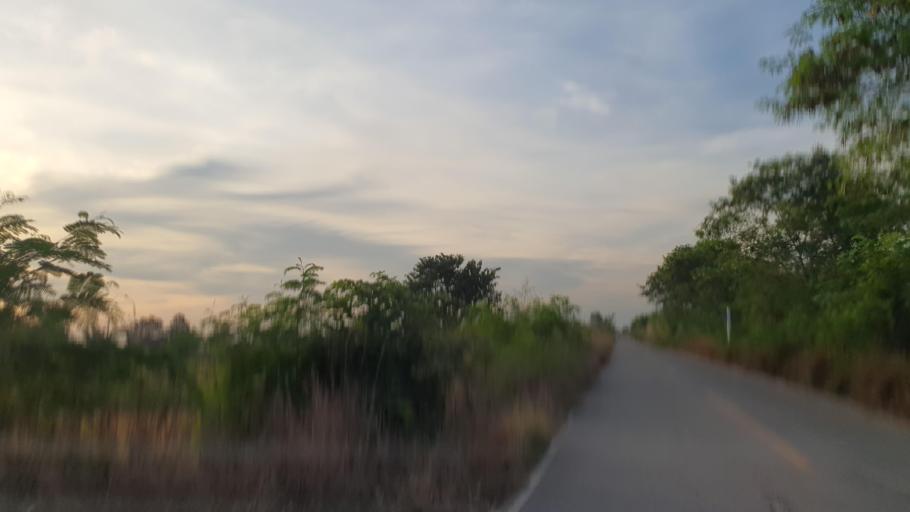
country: TH
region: Uthai Thani
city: Sawang Arom
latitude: 15.6974
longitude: 99.9601
